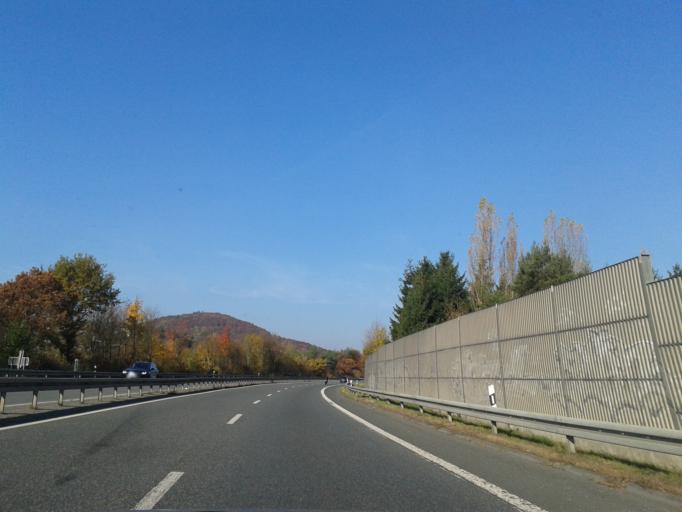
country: DE
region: Hesse
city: Herborn
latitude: 50.6894
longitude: 8.3074
